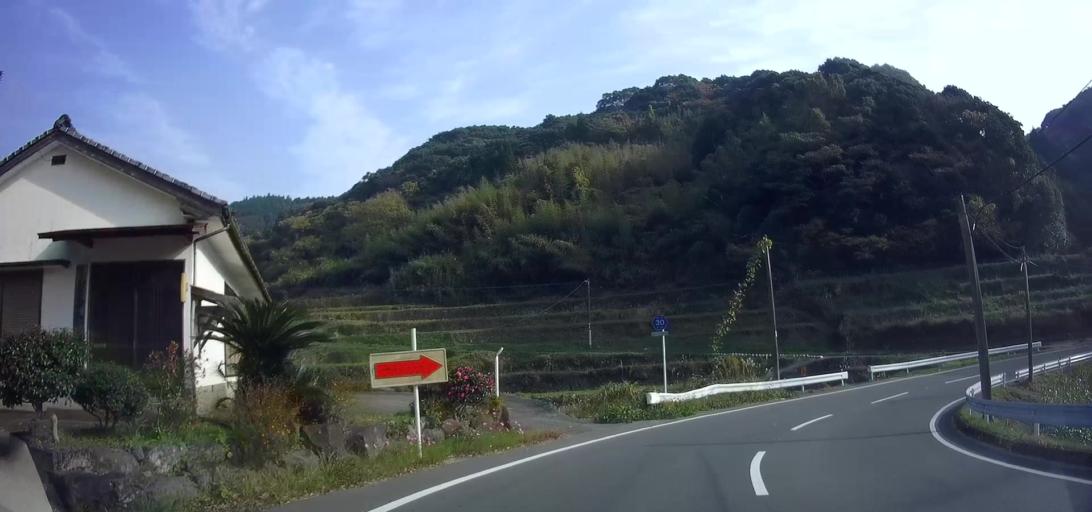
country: JP
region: Nagasaki
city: Shimabara
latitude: 32.6722
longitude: 130.2175
